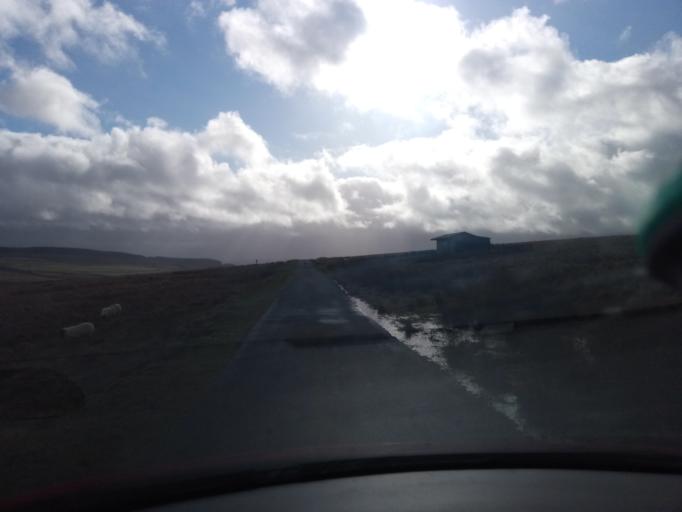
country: GB
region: England
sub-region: Northumberland
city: Rochester
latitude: 55.3123
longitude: -2.2863
